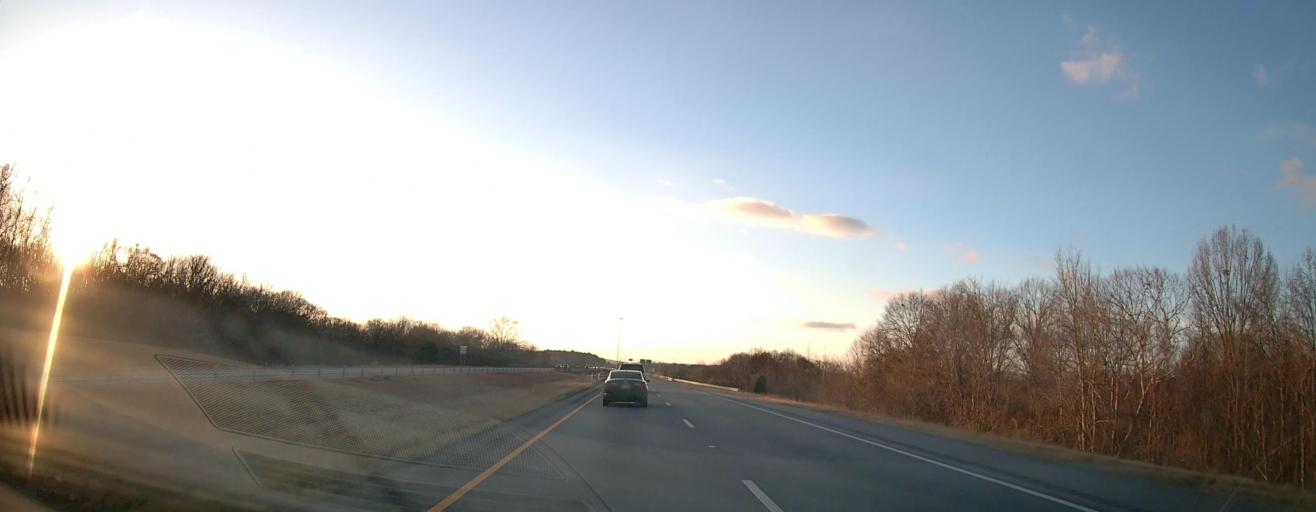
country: US
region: Alabama
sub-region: Etowah County
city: Attalla
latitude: 34.0039
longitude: -86.0661
